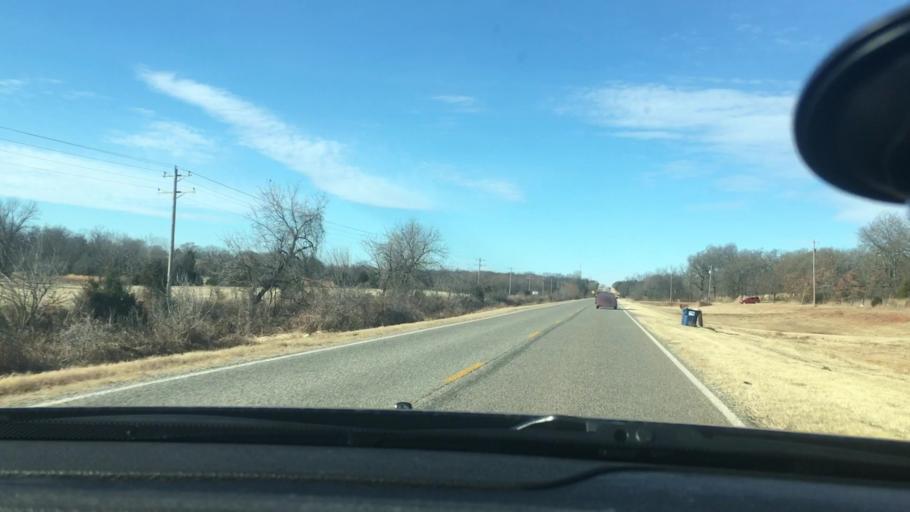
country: US
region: Oklahoma
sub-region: Cleveland County
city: Lexington
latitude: 35.0149
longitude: -97.1521
